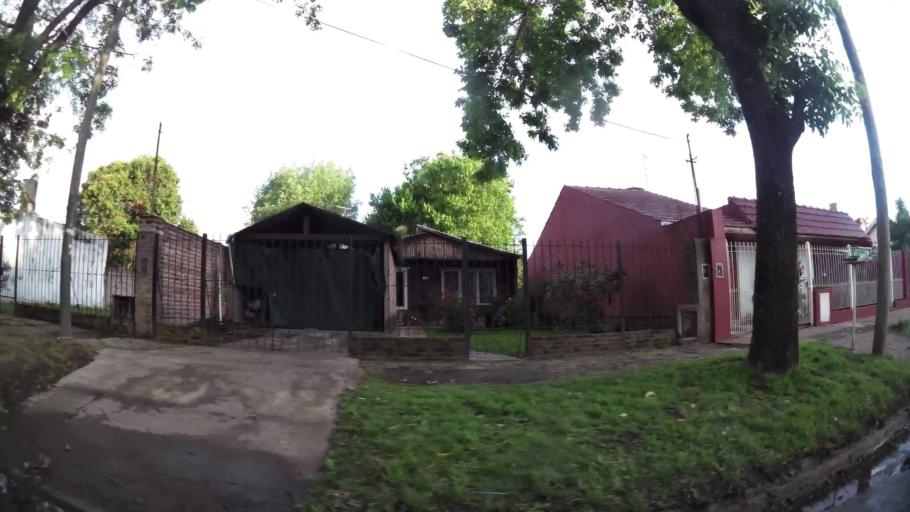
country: AR
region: Buenos Aires
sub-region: Partido de Almirante Brown
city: Adrogue
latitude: -34.7606
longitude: -58.3570
